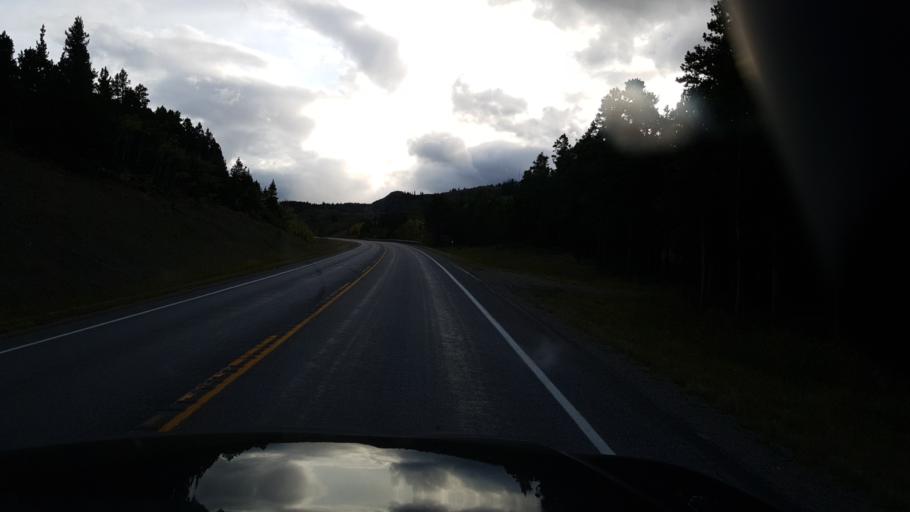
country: US
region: Montana
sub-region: Glacier County
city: South Browning
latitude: 48.4040
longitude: -113.2465
